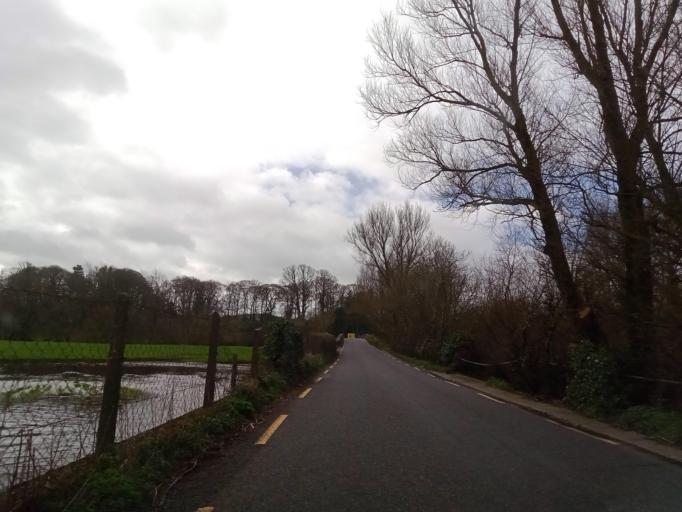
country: IE
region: Leinster
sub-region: Kilkenny
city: Ballyragget
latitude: 52.7148
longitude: -7.3220
